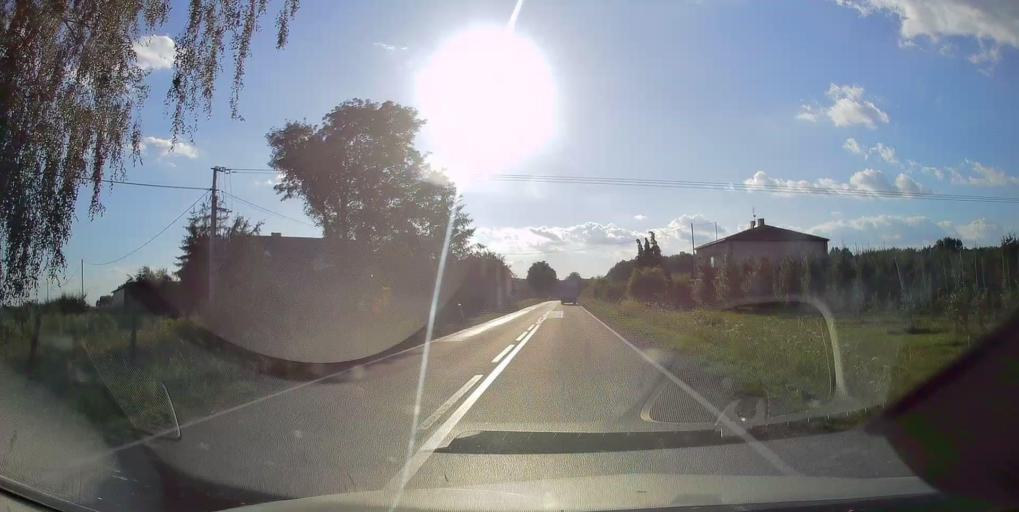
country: PL
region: Masovian Voivodeship
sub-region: Powiat grojecki
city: Bledow
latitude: 51.8030
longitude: 20.6007
